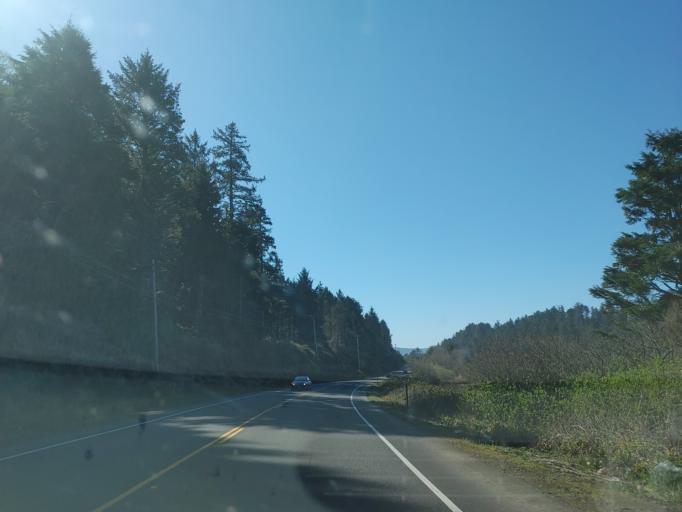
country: US
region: Oregon
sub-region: Tillamook County
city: Rockaway Beach
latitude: 45.5821
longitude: -123.9458
